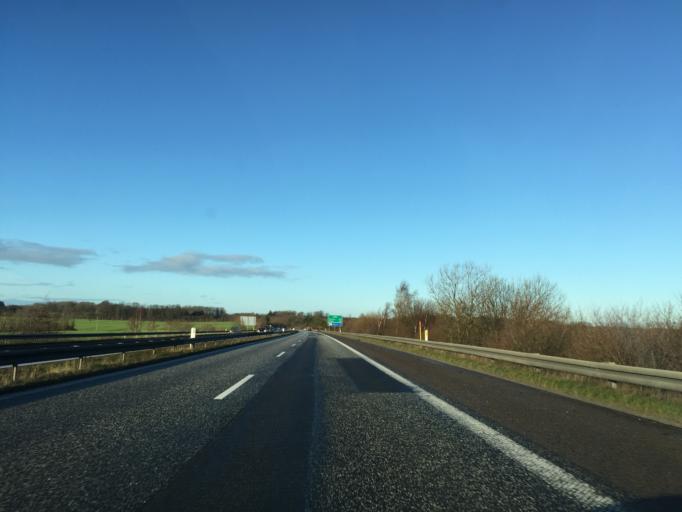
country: DK
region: South Denmark
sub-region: Fredericia Kommune
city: Taulov
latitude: 55.5498
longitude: 9.6398
